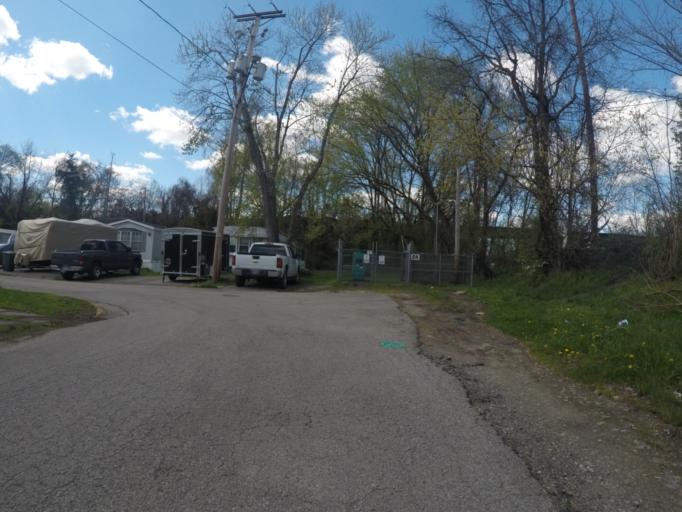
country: US
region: West Virginia
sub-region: Wayne County
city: Kenova
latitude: 38.3972
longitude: -82.5764
